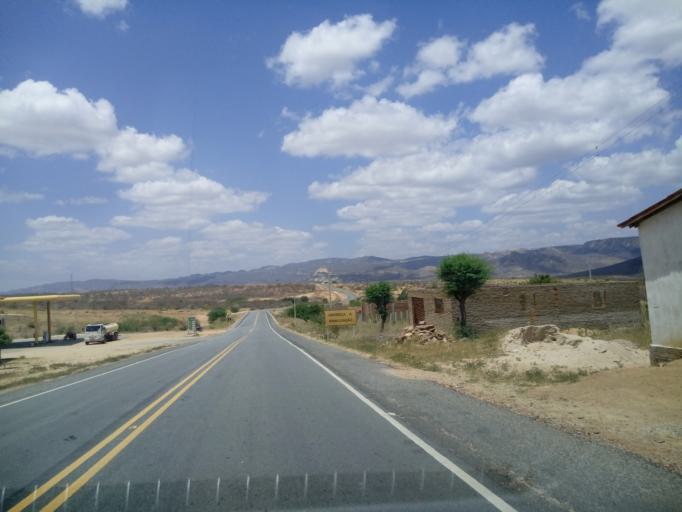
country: BR
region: Paraiba
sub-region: Desterro
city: Desterro
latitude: -7.1202
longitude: -37.0638
